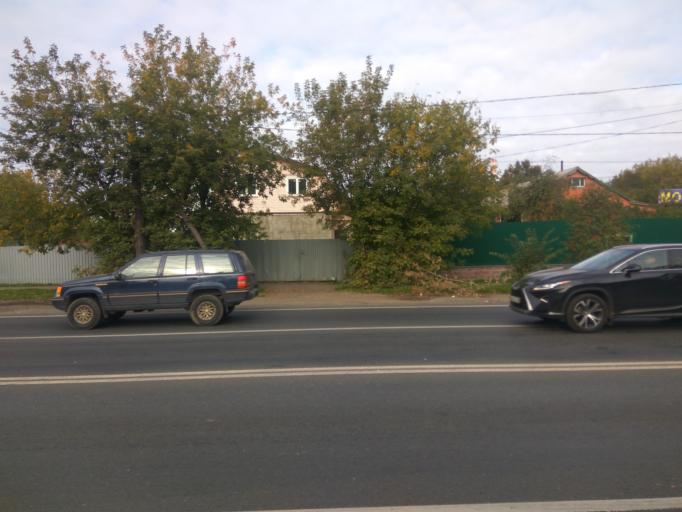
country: RU
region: Moskovskaya
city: Medvezh'i Ozera
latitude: 55.8617
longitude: 37.9868
